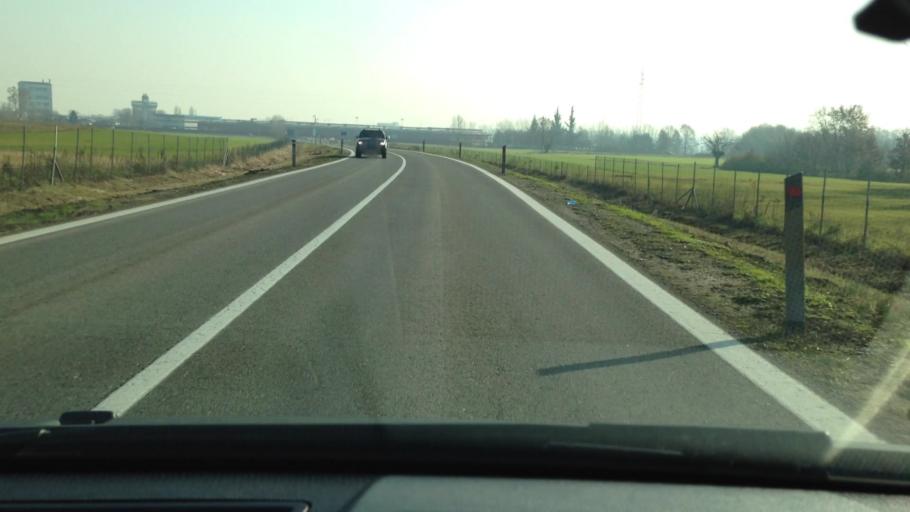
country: IT
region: Piedmont
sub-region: Provincia di Alessandria
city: Quattordio
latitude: 44.9030
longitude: 8.4159
